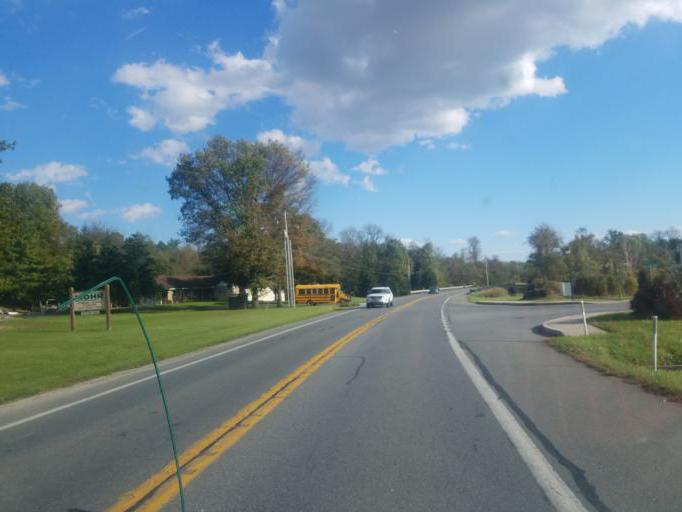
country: US
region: Pennsylvania
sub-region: Lancaster County
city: Bainbridge
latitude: 40.0995
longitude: -76.6691
